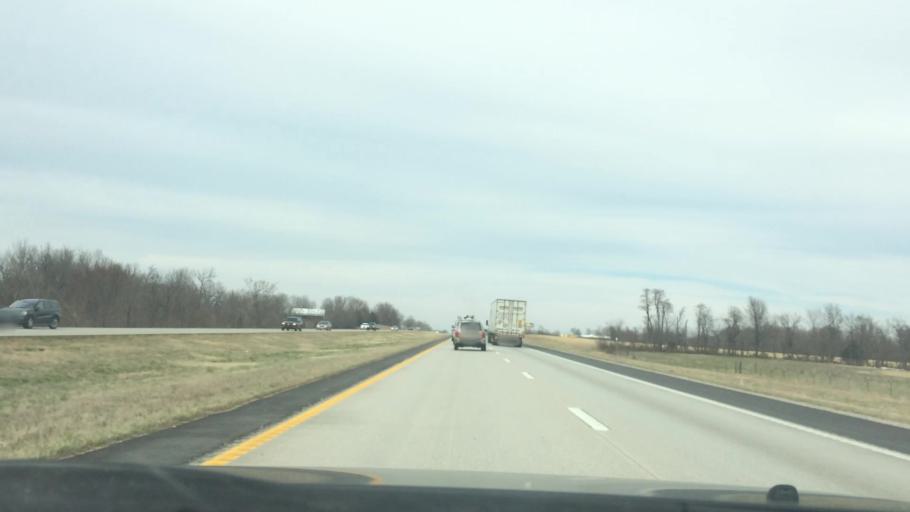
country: US
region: Missouri
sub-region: Greene County
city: Willard
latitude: 37.4522
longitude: -93.3549
